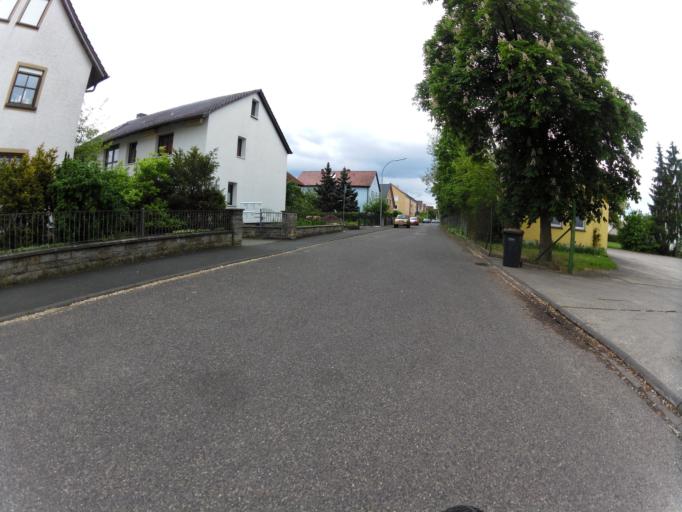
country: DE
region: Bavaria
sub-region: Regierungsbezirk Unterfranken
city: Volkach
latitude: 49.8643
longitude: 10.2373
